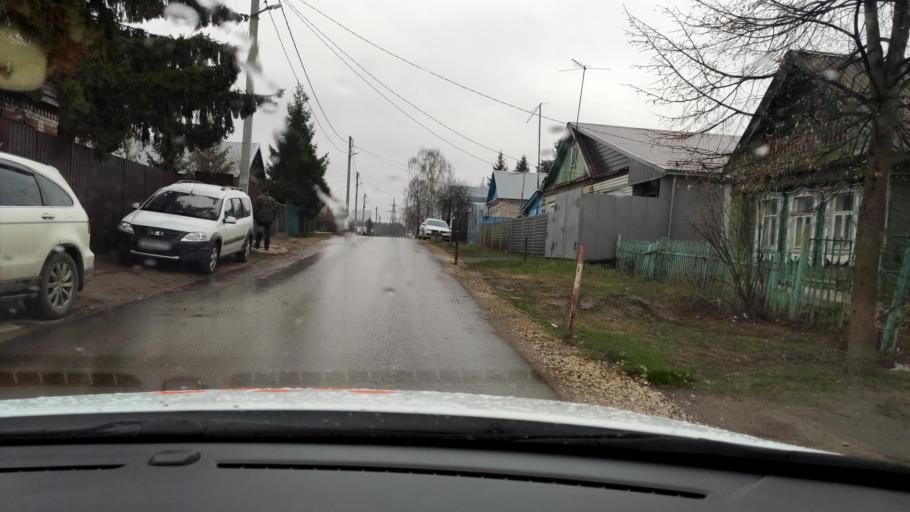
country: RU
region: Tatarstan
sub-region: Gorod Kazan'
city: Kazan
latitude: 55.7251
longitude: 49.1453
